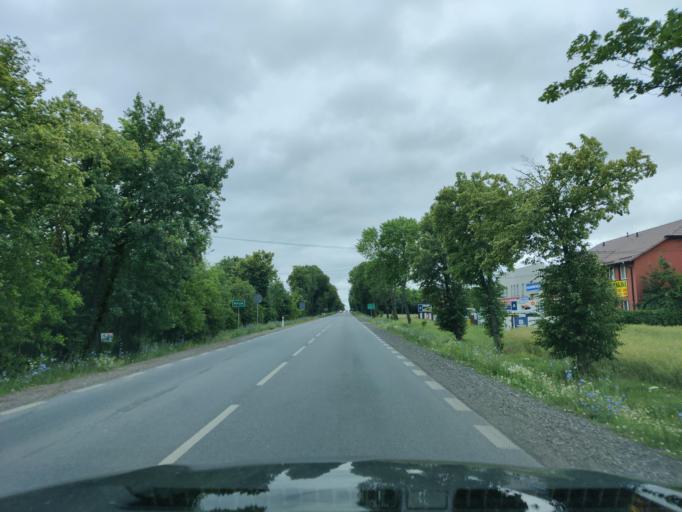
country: PL
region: Masovian Voivodeship
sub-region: Powiat pultuski
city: Pultusk
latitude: 52.6865
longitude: 21.0806
